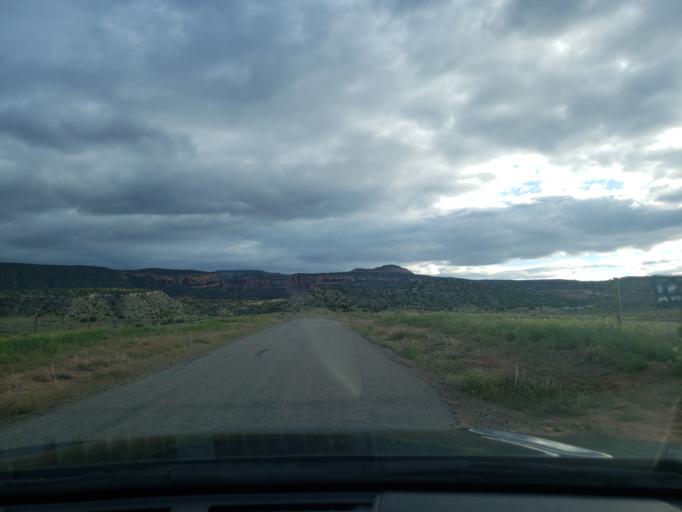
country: US
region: Colorado
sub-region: Mesa County
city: Fruita
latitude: 39.1419
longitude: -108.7477
